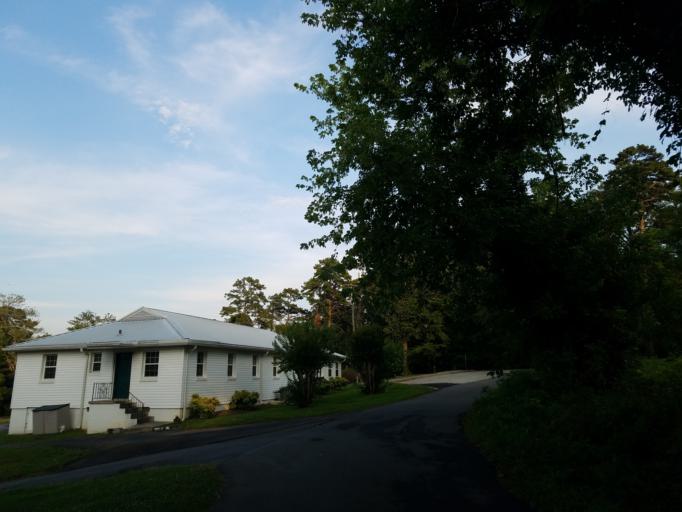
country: US
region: Georgia
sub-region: Pickens County
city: Nelson
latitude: 34.4164
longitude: -84.3871
